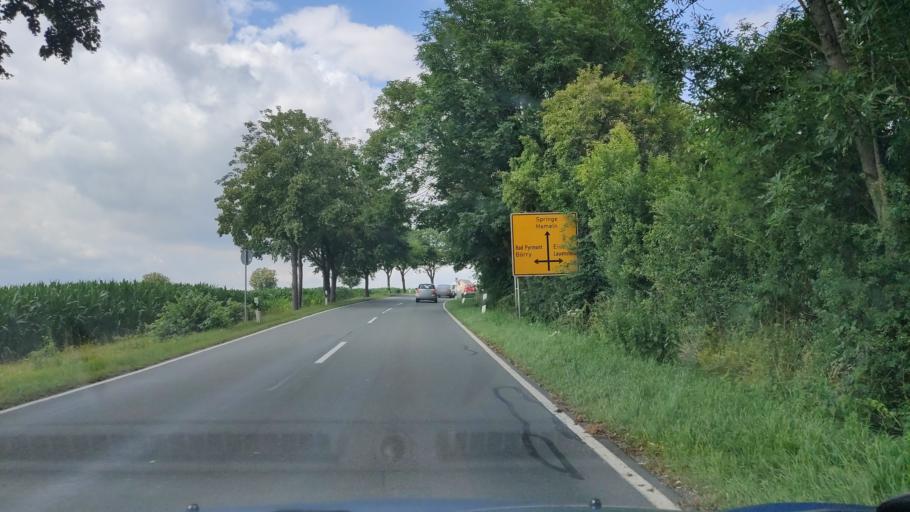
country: DE
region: Lower Saxony
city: Heyen
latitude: 52.0601
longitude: 9.5256
